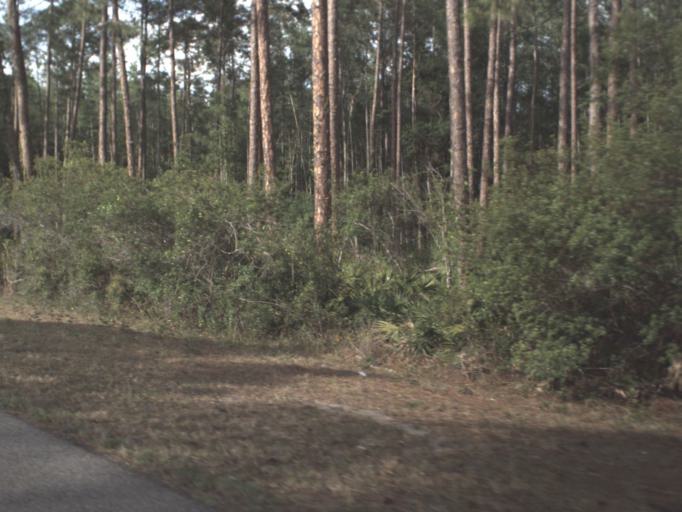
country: US
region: Florida
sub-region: Hernando County
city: Ridge Manor
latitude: 28.5191
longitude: -82.0545
